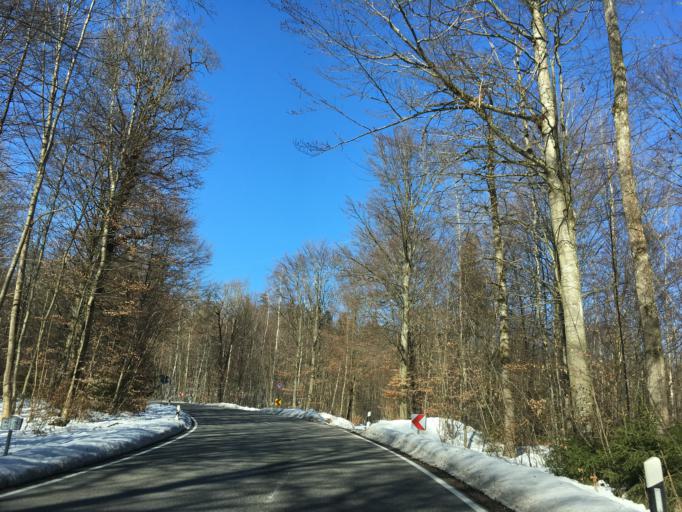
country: DE
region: Bavaria
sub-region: Upper Bavaria
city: Maitenbeth
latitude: 48.1253
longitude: 12.0877
